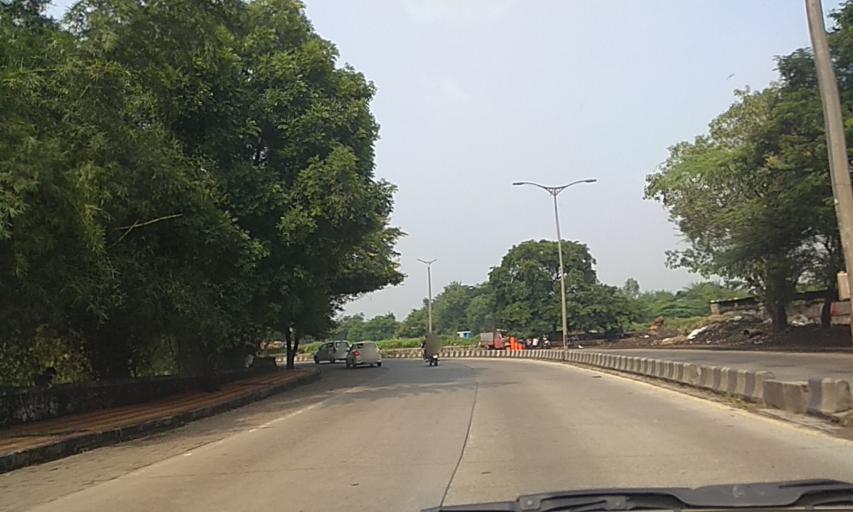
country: IN
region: Maharashtra
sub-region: Pune Division
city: Khadki
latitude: 18.5504
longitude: 73.8529
